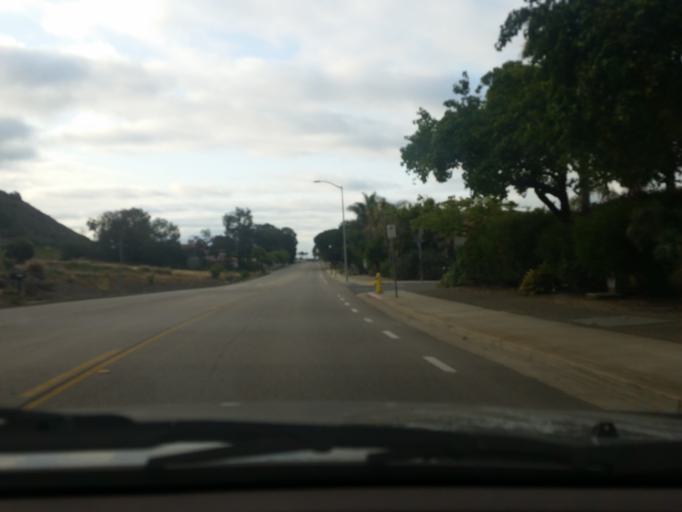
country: US
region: California
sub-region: San Luis Obispo County
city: Avila Beach
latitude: 35.1692
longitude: -120.6928
